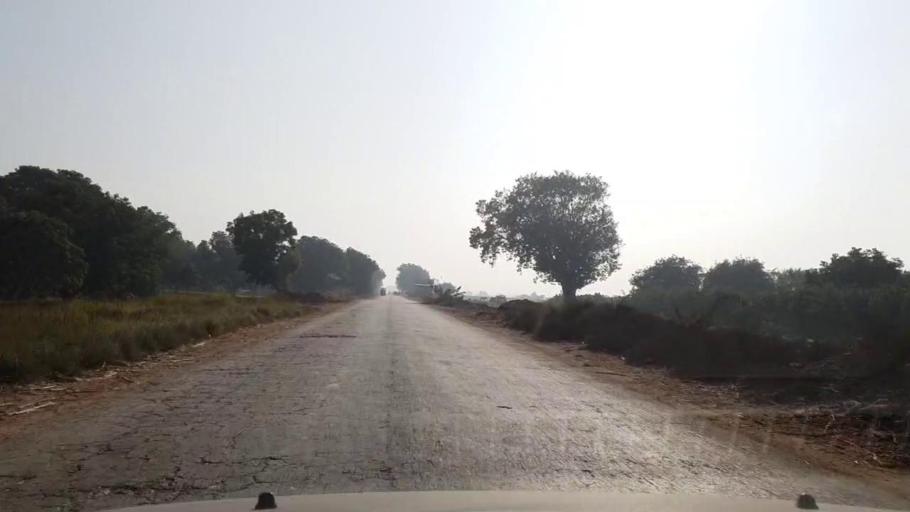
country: PK
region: Sindh
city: Matiari
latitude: 25.5901
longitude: 68.4770
